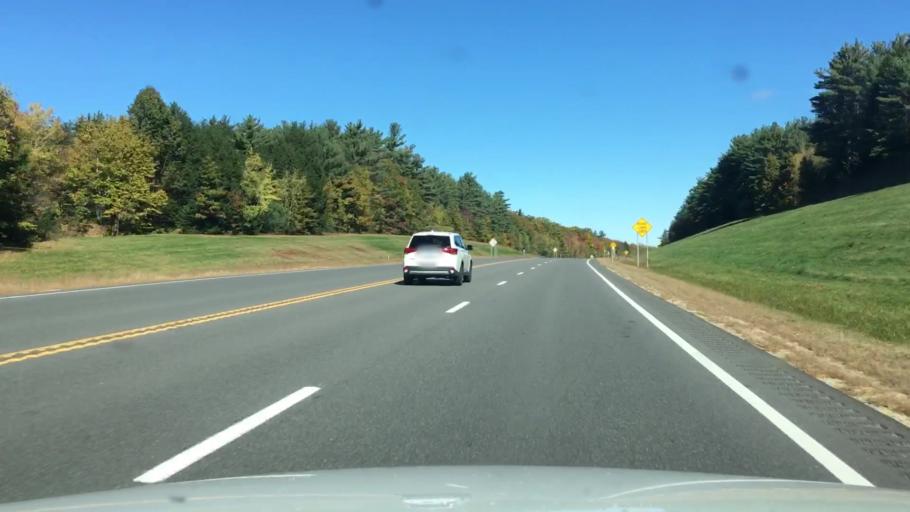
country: US
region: New Hampshire
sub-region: Strafford County
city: Farmington
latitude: 43.4283
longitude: -71.0096
